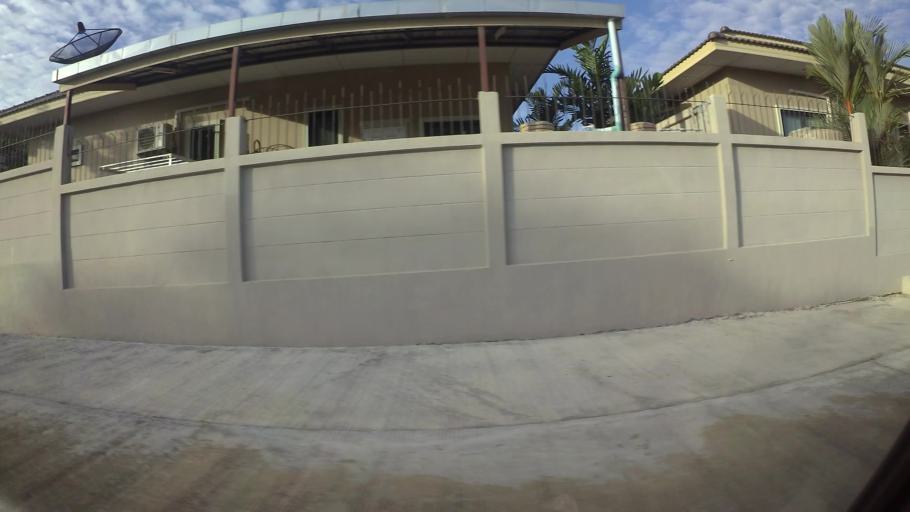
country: TH
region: Chon Buri
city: Sattahip
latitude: 12.7290
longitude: 100.9153
